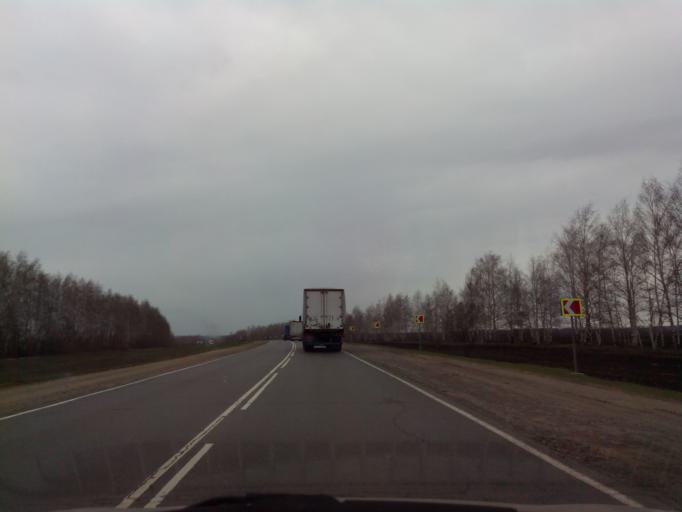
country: RU
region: Tambov
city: Pokrovo-Prigorodnoye
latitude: 52.6663
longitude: 41.3387
